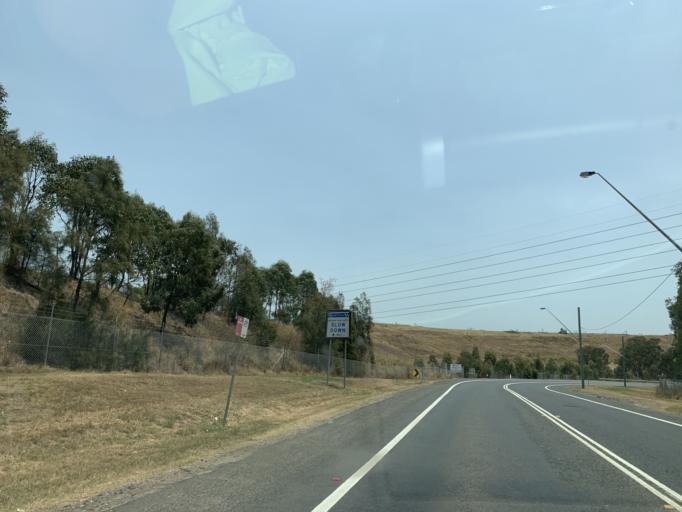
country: AU
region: New South Wales
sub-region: Fairfield
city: Horsley Park
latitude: -33.8157
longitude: 150.8665
